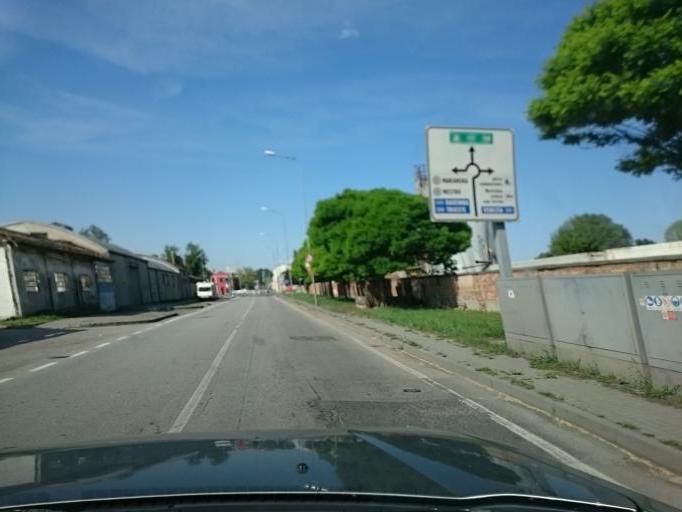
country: IT
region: Veneto
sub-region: Provincia di Venezia
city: Mestre
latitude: 45.4745
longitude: 12.2340
